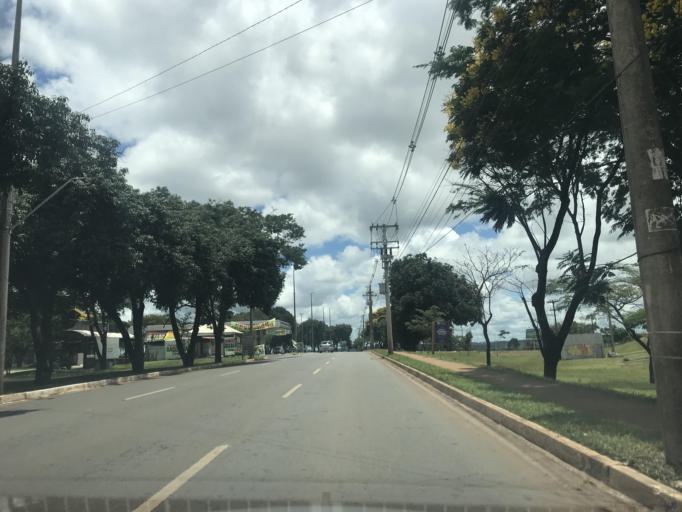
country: BR
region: Federal District
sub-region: Brasilia
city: Brasilia
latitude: -15.6516
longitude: -47.7843
